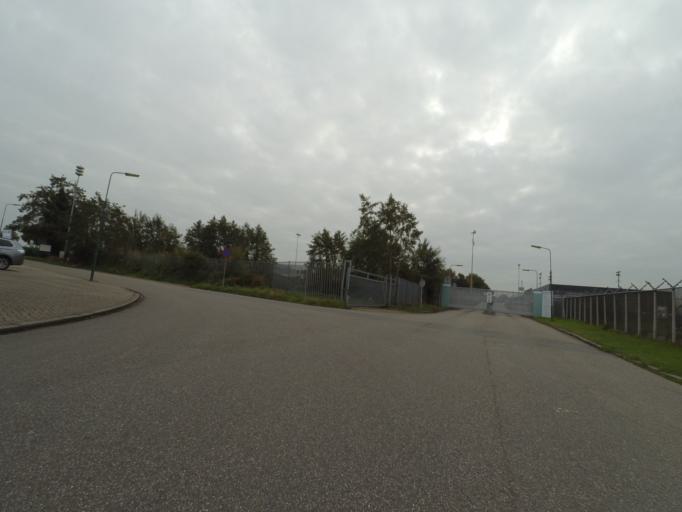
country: NL
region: Utrecht
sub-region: Gemeente Leusden
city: Leusden
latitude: 52.1199
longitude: 5.4208
